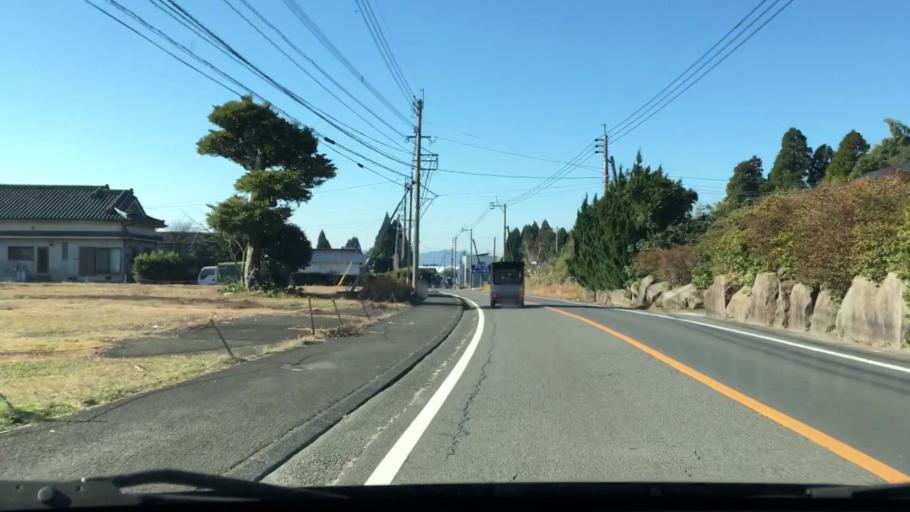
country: JP
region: Kagoshima
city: Kajiki
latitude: 31.7892
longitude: 130.7113
